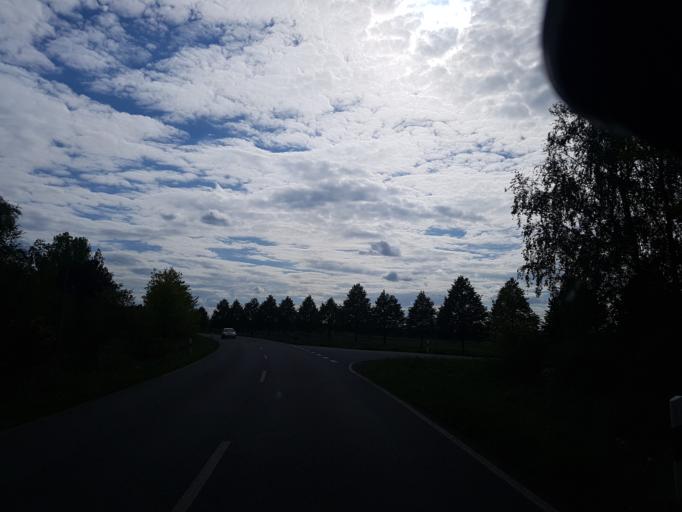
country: DE
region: Brandenburg
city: Grossraschen
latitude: 51.5789
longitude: 13.9618
